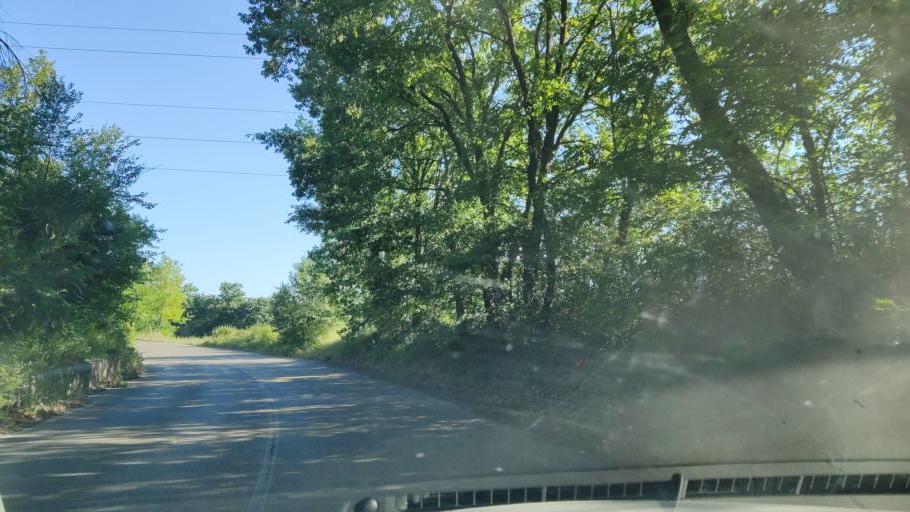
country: IT
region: Umbria
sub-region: Provincia di Terni
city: Penna in Teverina
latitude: 42.4754
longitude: 12.3645
